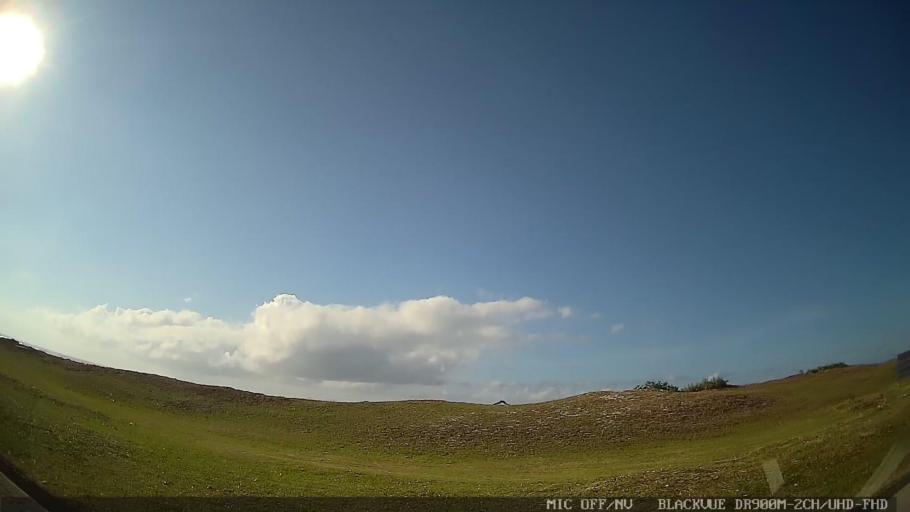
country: BR
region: Sao Paulo
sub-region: Peruibe
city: Peruibe
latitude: -24.2789
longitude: -46.9405
